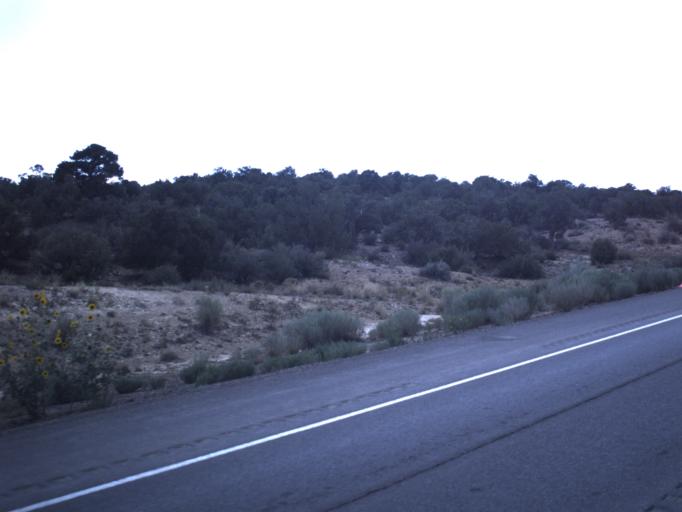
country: US
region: Utah
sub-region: Duchesne County
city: Duchesne
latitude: 40.1658
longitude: -110.4758
